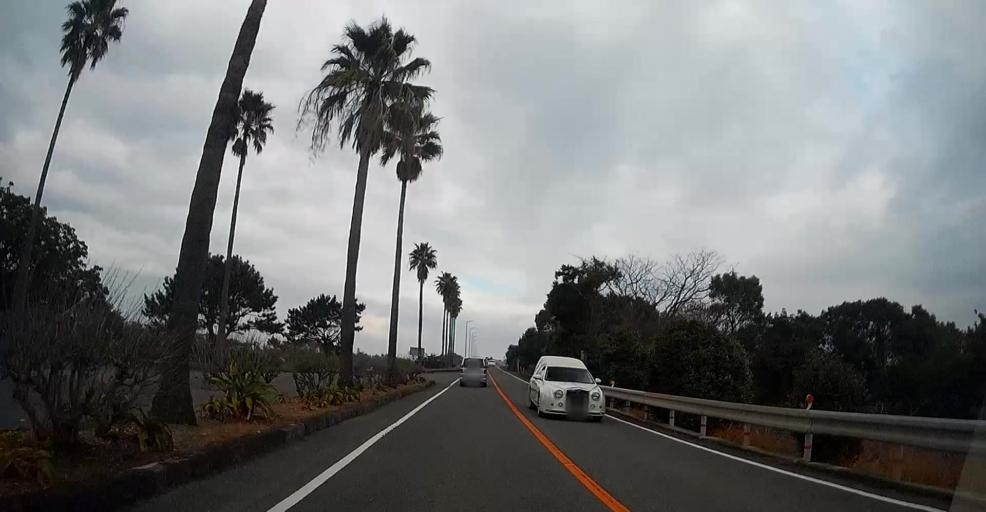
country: JP
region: Kumamoto
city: Yatsushiro
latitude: 32.5351
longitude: 130.4226
